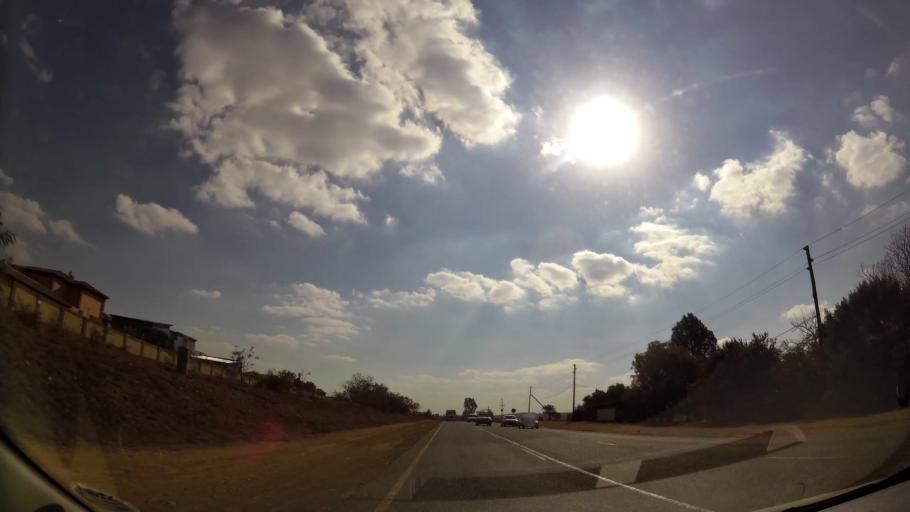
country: ZA
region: Gauteng
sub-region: West Rand District Municipality
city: Muldersdriseloop
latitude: -26.0568
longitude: 27.8257
